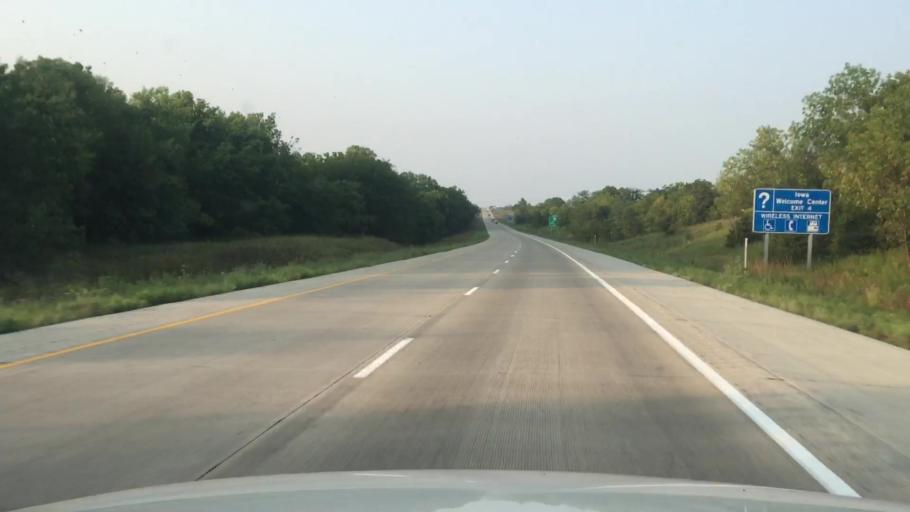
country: US
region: Iowa
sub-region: Decatur County
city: Lamoni
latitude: 40.6034
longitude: -93.9051
